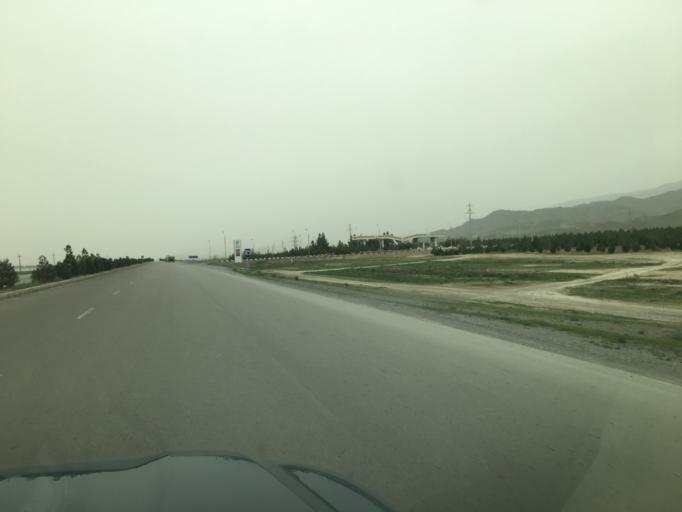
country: TM
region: Ahal
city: Baharly
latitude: 38.2763
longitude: 57.6842
